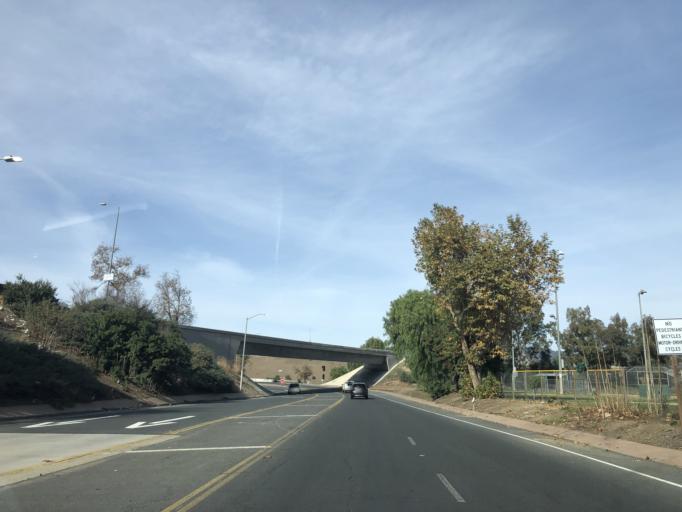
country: US
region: California
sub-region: Los Angeles County
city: San Fernando
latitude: 34.2640
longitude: -118.4403
